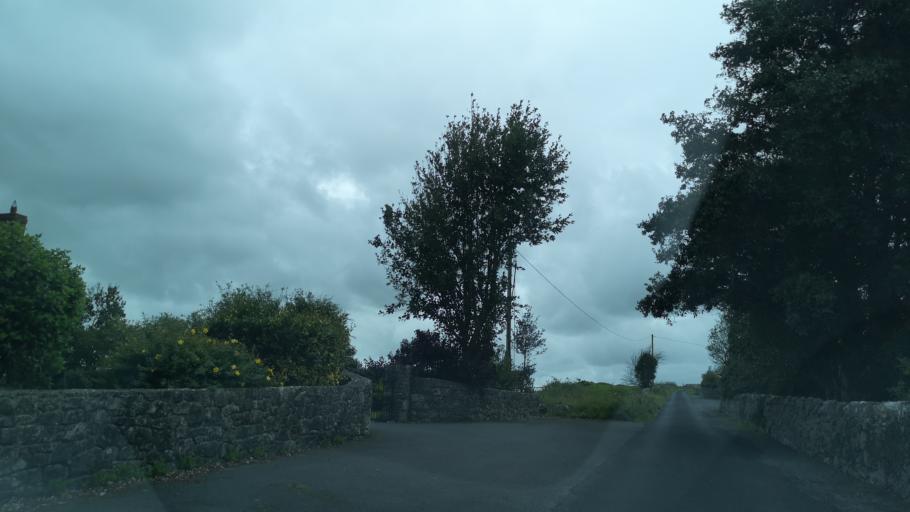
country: IE
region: Connaught
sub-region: County Galway
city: Athenry
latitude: 53.3103
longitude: -8.7423
